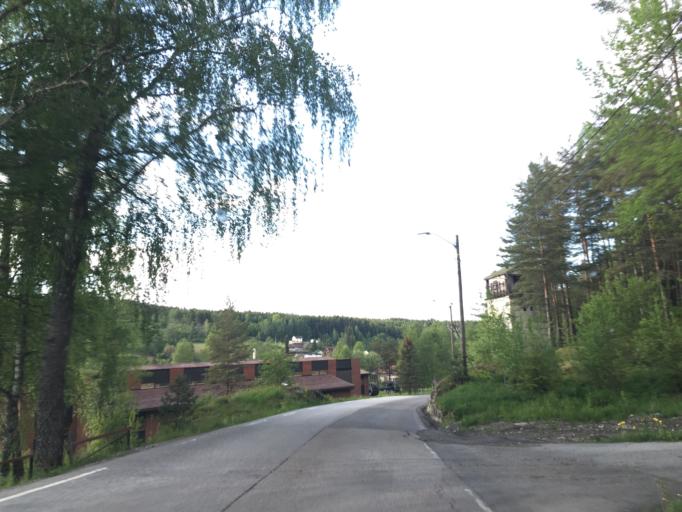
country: NO
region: Akershus
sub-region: Nes
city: Auli
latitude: 60.0271
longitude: 11.3276
